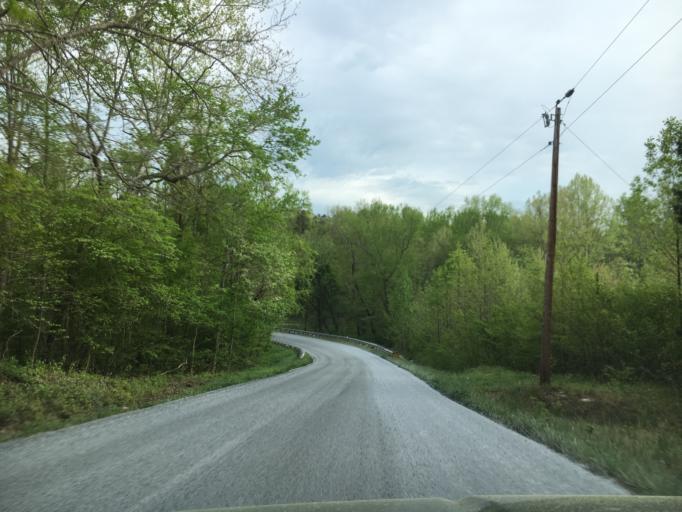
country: US
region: Virginia
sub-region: Campbell County
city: Brookneal
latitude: 36.9446
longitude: -78.9522
